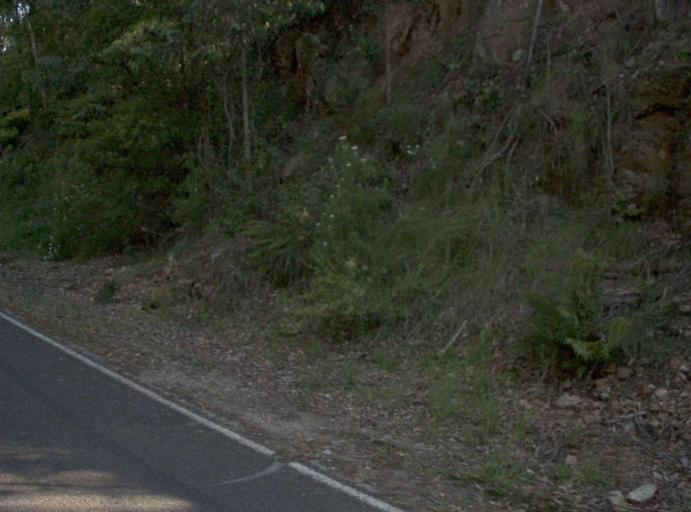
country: AU
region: Victoria
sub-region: East Gippsland
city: Lakes Entrance
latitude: -37.6440
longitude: 148.4807
